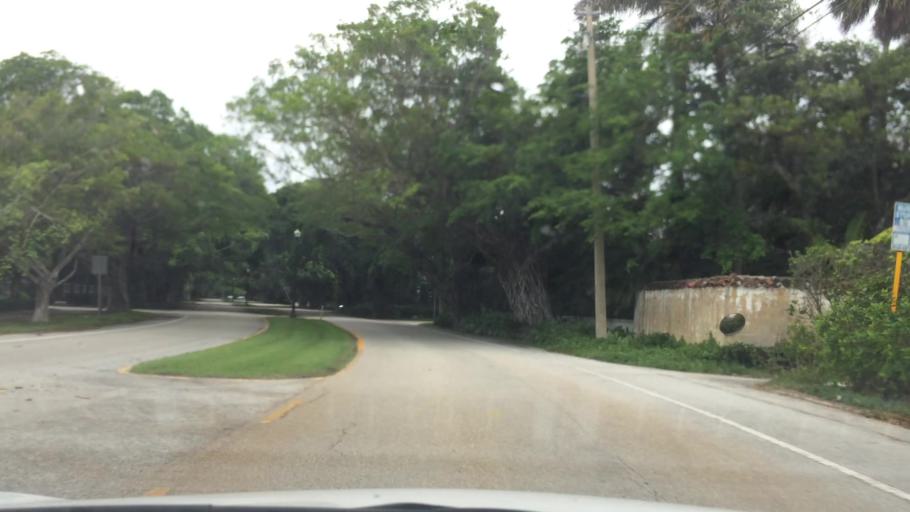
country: US
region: Florida
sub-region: Palm Beach County
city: West Palm Beach
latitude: 26.7276
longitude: -80.0377
